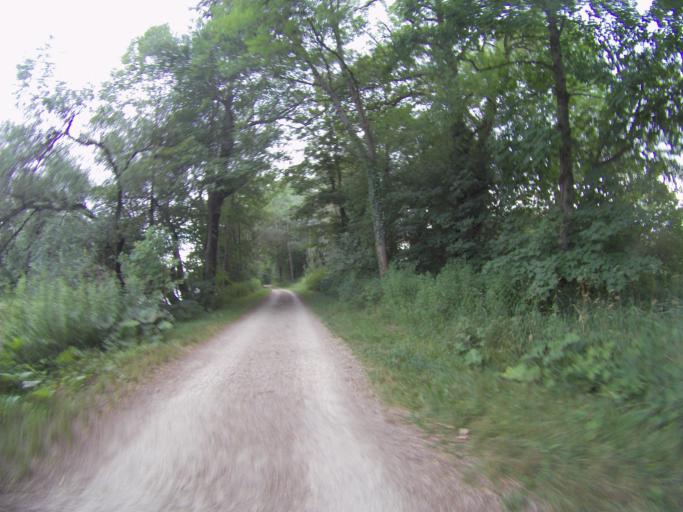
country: DE
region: Bavaria
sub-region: Upper Bavaria
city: Freising
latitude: 48.4048
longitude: 11.7637
